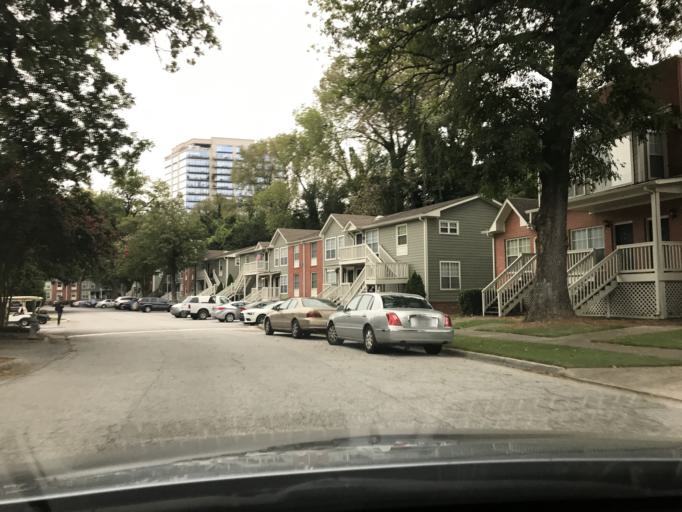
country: US
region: Georgia
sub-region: DeKalb County
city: Druid Hills
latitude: 33.8134
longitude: -84.3891
